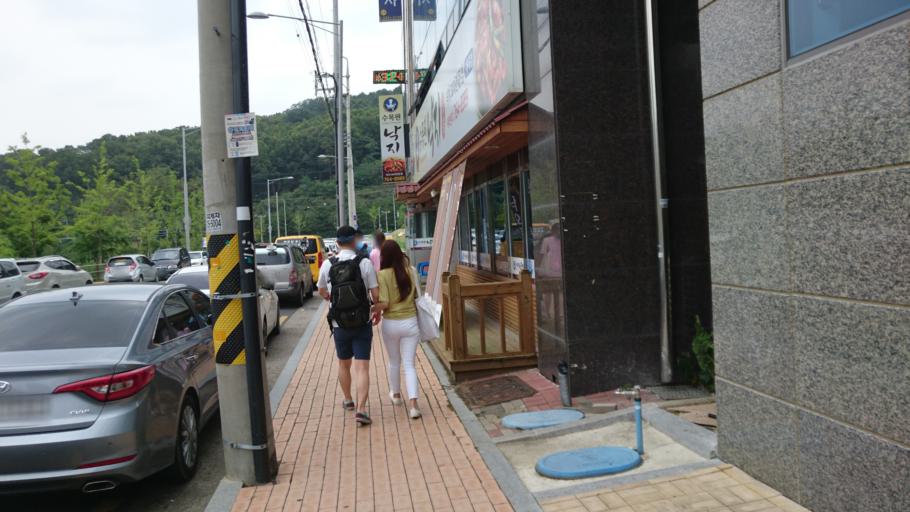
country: KR
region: Daegu
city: Hwawon
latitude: 35.8049
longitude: 128.5191
